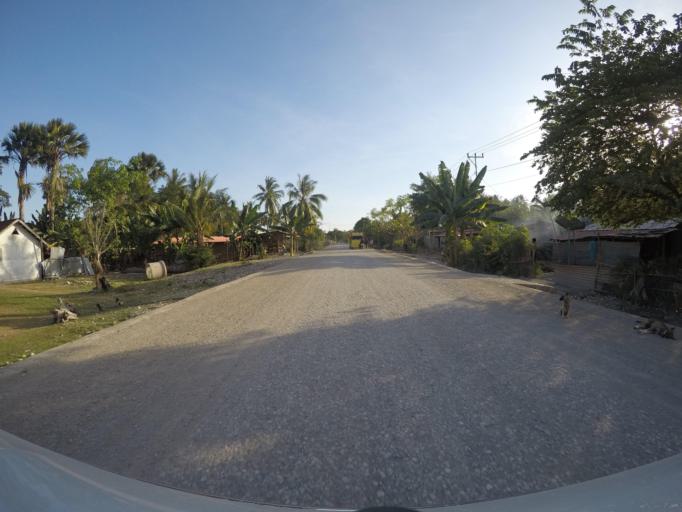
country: TL
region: Viqueque
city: Viqueque
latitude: -8.8131
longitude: 126.5373
